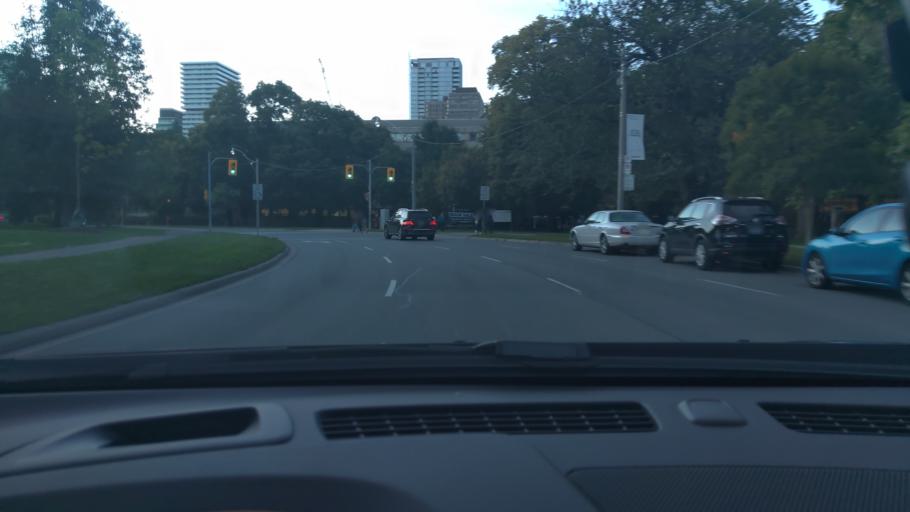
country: CA
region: Ontario
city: Toronto
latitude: 43.6655
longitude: -79.3914
